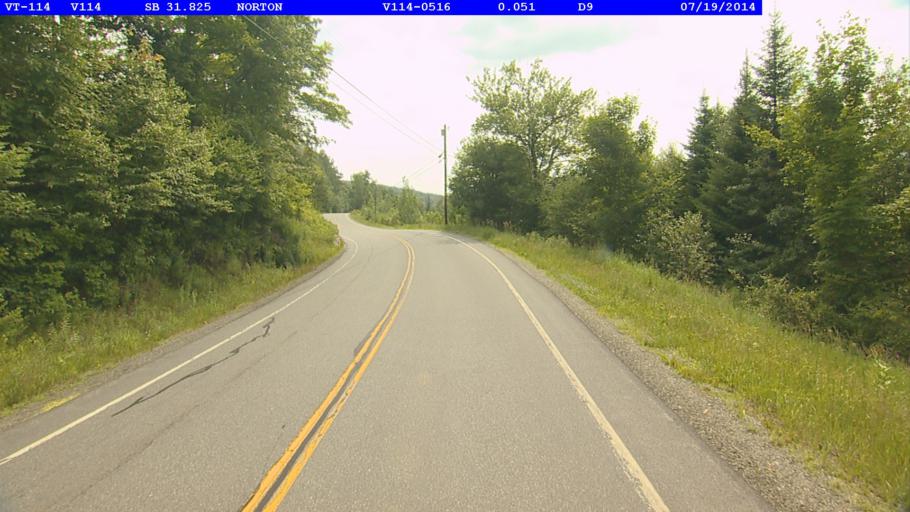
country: CA
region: Quebec
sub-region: Estrie
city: Coaticook
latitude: 44.9466
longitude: -71.8474
